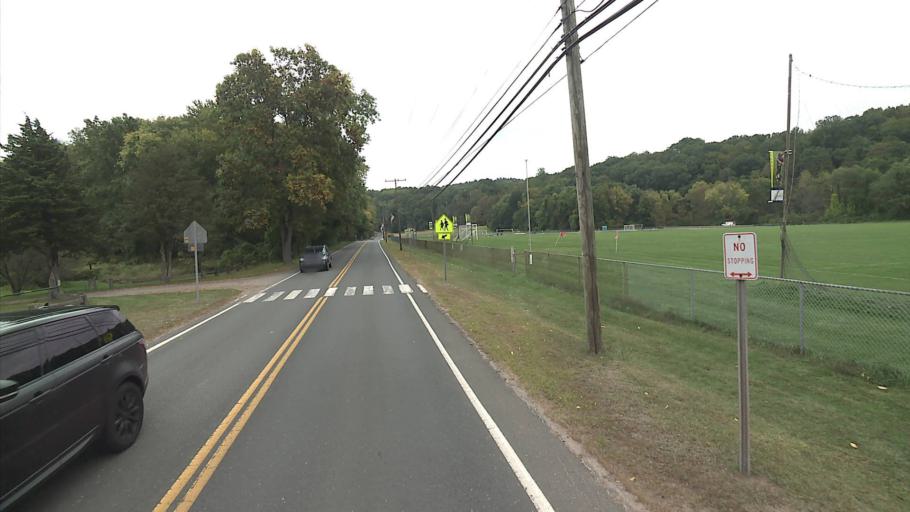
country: US
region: Connecticut
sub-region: Hartford County
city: Tariffville
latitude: 41.8964
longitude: -72.7784
